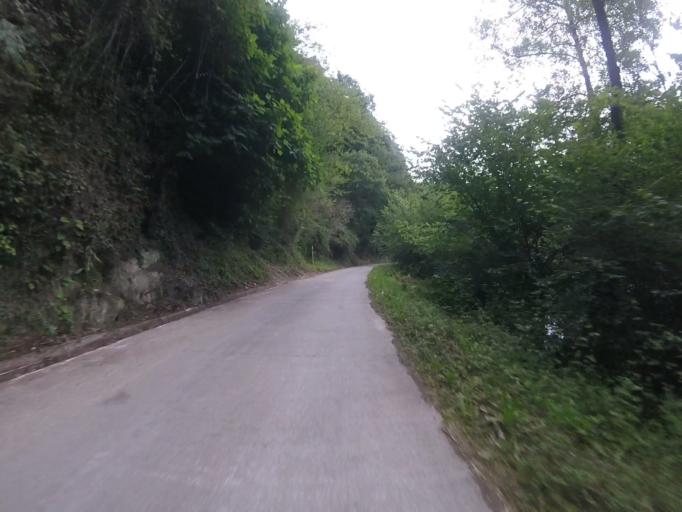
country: ES
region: Navarre
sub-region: Provincia de Navarra
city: Sunbilla
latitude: 43.1744
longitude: -1.6773
